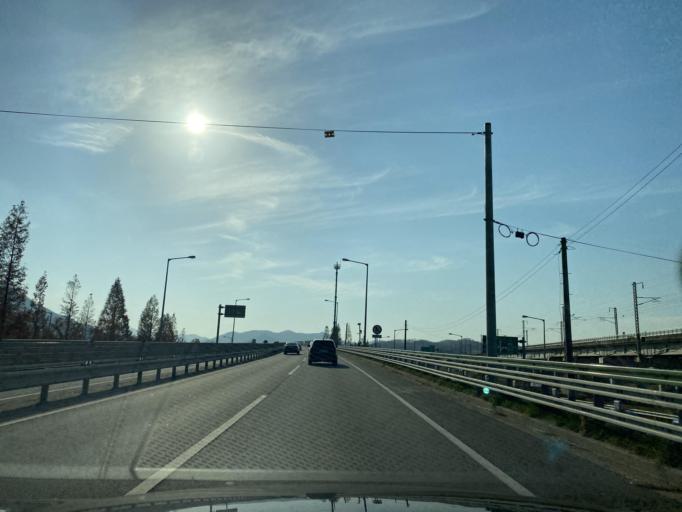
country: KR
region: Chungcheongnam-do
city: Asan
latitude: 36.7738
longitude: 127.0449
